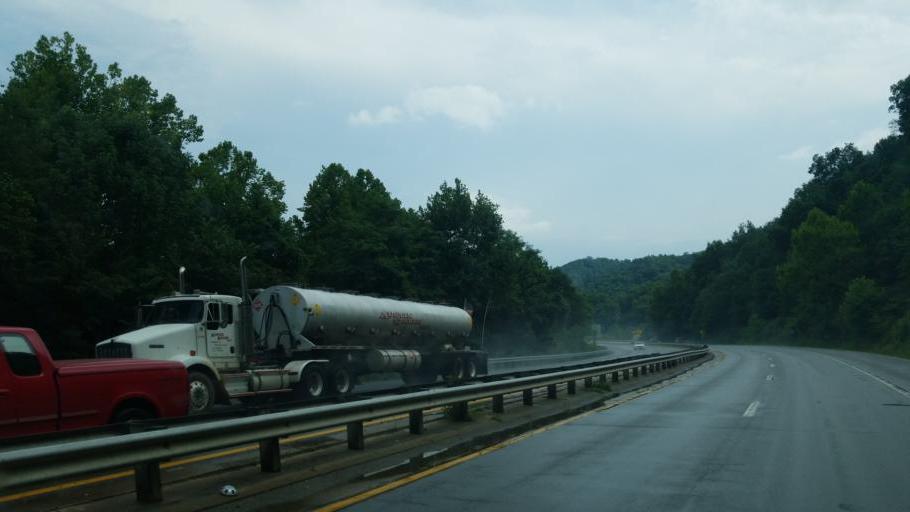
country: US
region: West Virginia
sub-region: Logan County
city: Chapmanville
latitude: 37.9679
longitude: -82.0233
